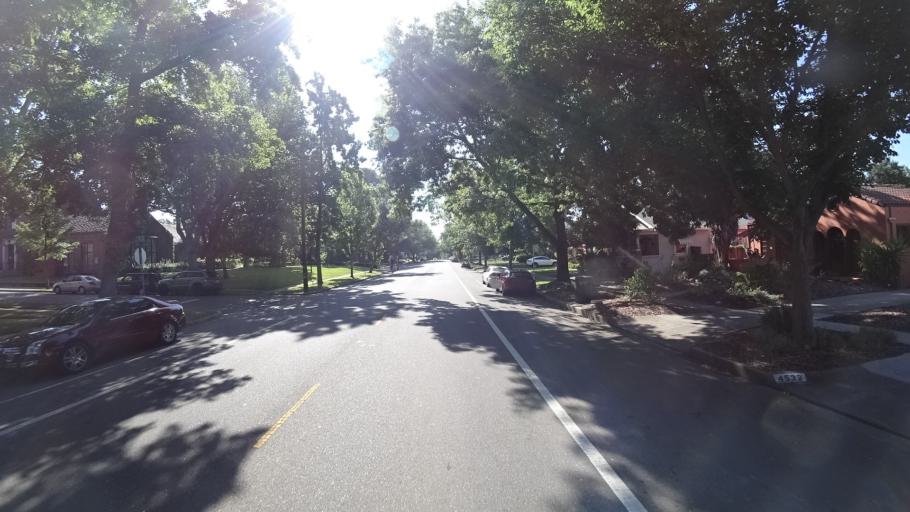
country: US
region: California
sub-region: Sacramento County
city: Sacramento
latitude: 38.5566
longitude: -121.4519
